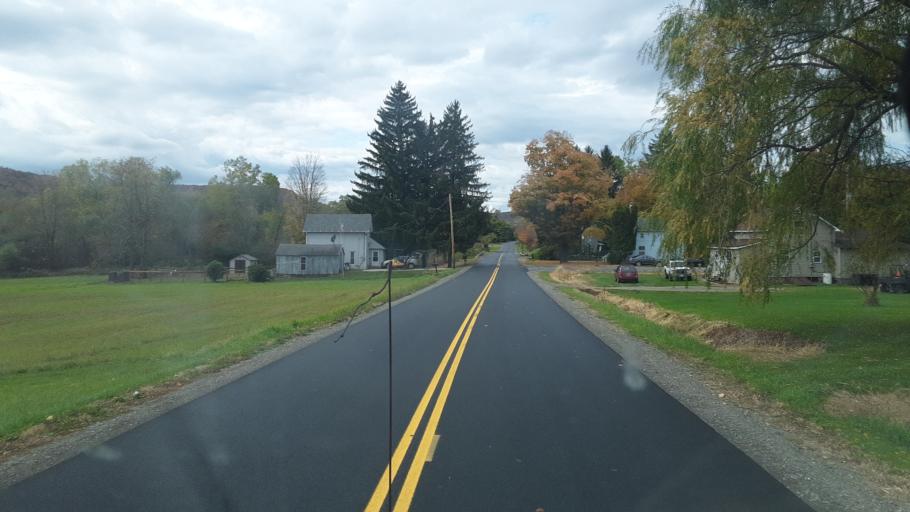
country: US
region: New York
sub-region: Allegany County
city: Alfred
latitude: 42.3662
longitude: -77.7728
